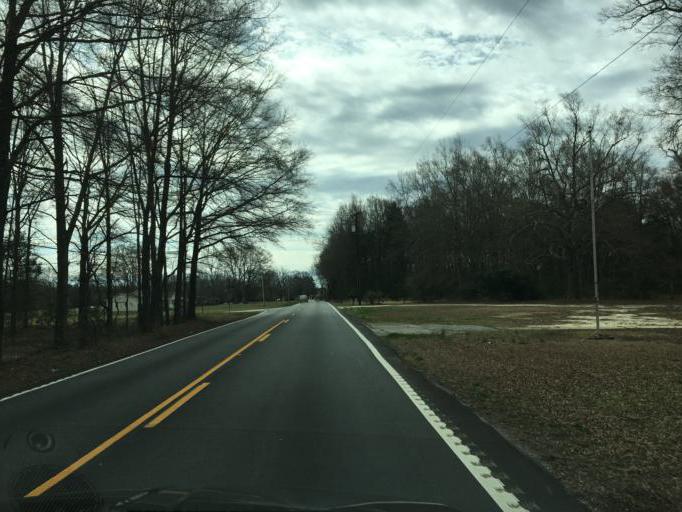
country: US
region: South Carolina
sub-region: Greenville County
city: Fountain Inn
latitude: 34.6814
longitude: -82.2199
